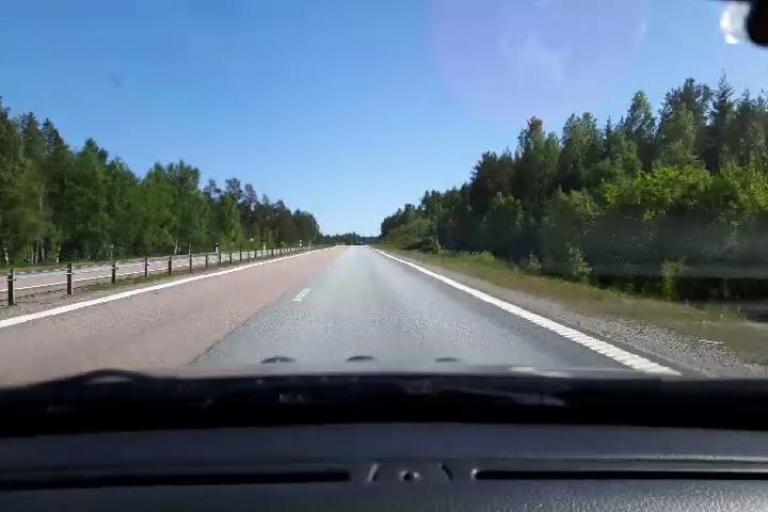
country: SE
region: Gaevleborg
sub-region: Soderhamns Kommun
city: Soderhamn
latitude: 61.3255
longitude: 17.0274
